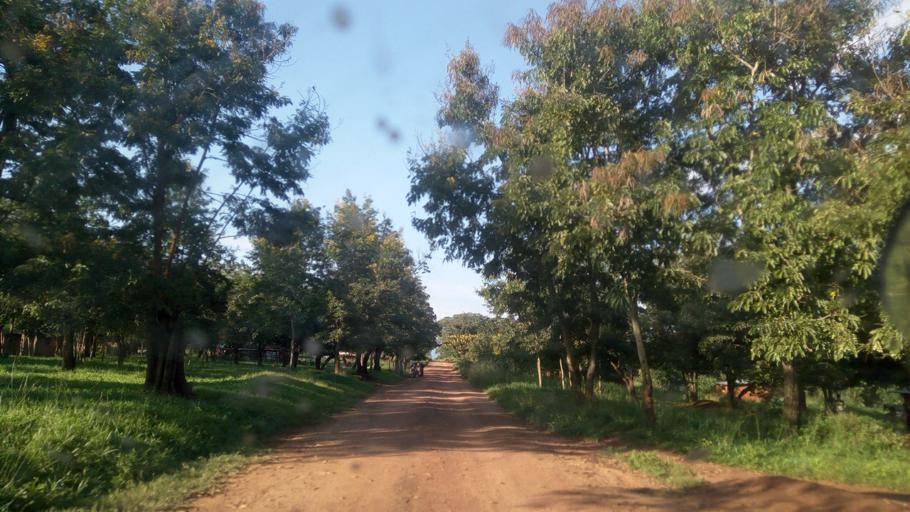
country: BI
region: Bururi
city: Rumonge
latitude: -4.2527
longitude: 28.9876
